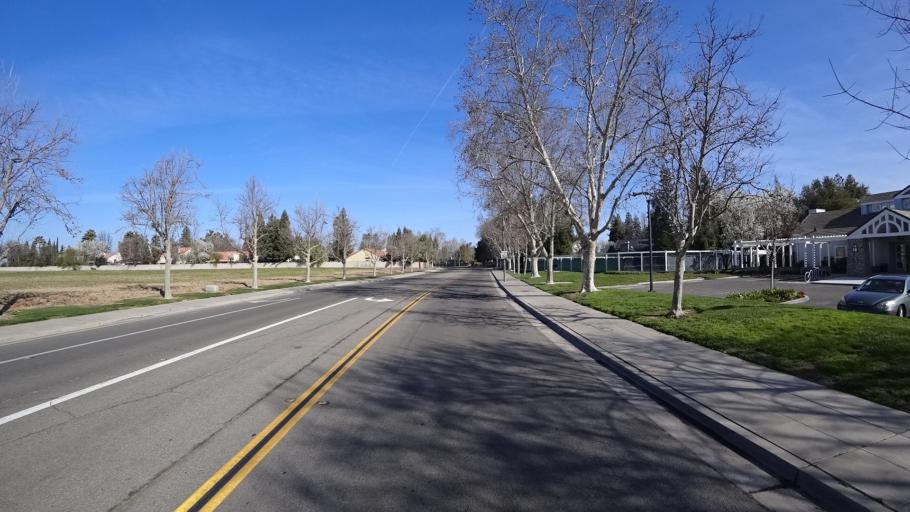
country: US
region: California
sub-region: Fresno County
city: Clovis
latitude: 36.8846
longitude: -119.7754
